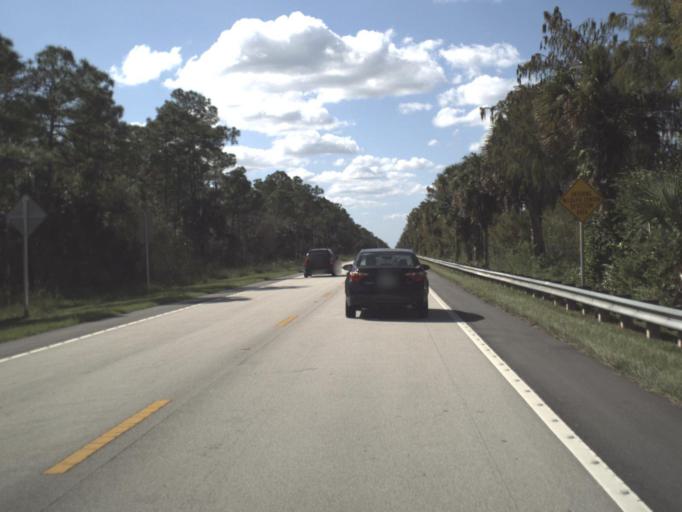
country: US
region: Florida
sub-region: Collier County
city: Marco
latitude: 25.8840
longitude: -81.2538
